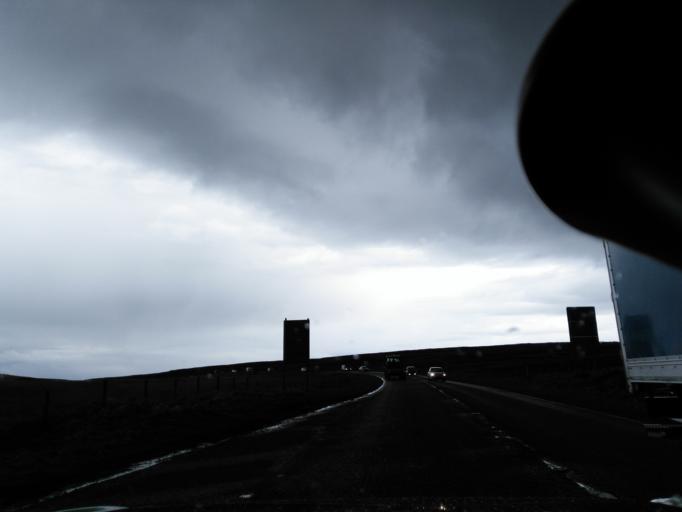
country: GB
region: England
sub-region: Bradford
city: Ilkley
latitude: 53.9900
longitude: -1.8068
